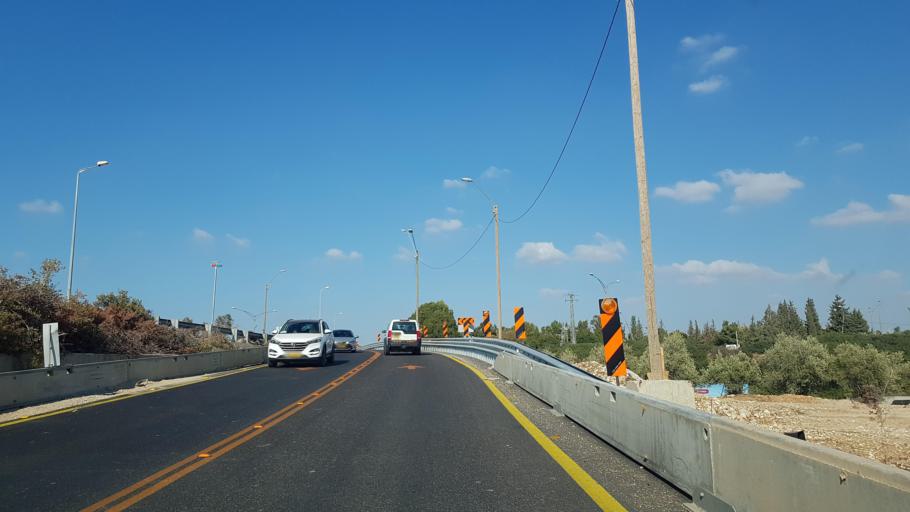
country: PS
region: West Bank
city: Tulkarm
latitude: 32.3357
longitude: 35.0076
